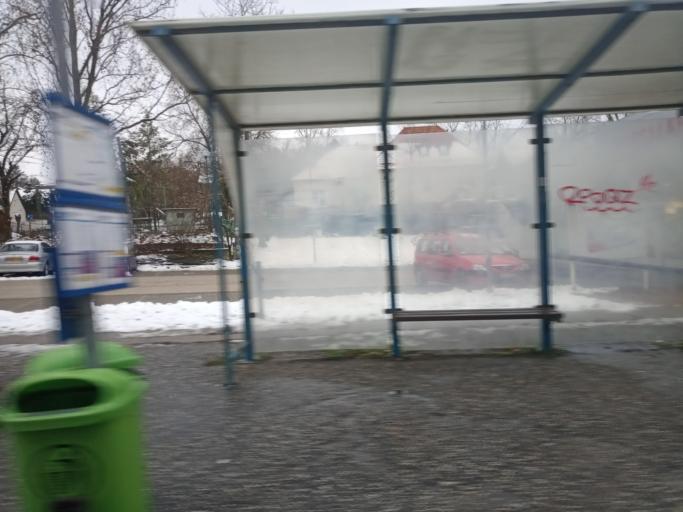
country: HU
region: Pest
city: Solymar
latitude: 47.5634
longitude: 18.9639
